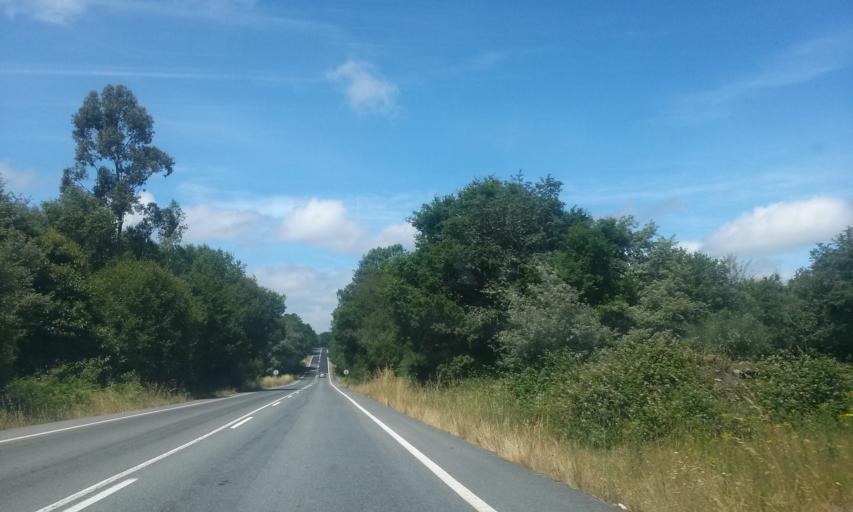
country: ES
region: Galicia
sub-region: Provincia de Lugo
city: Outeiro de Rei
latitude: 43.0157
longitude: -7.6634
